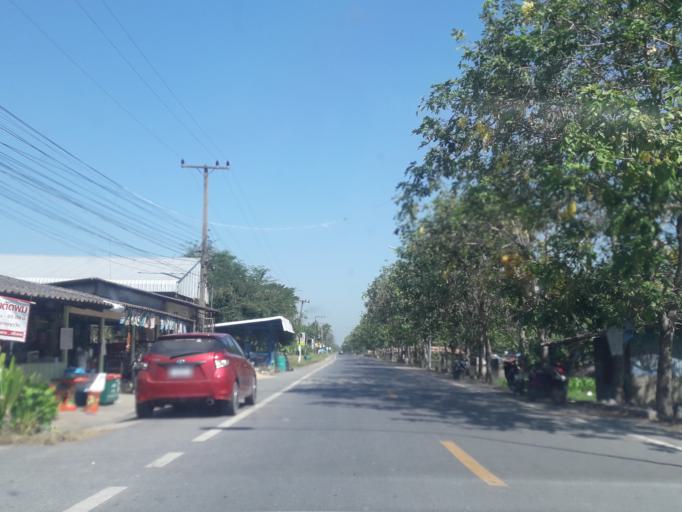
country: TH
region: Pathum Thani
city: Nong Suea
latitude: 14.1653
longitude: 100.8458
